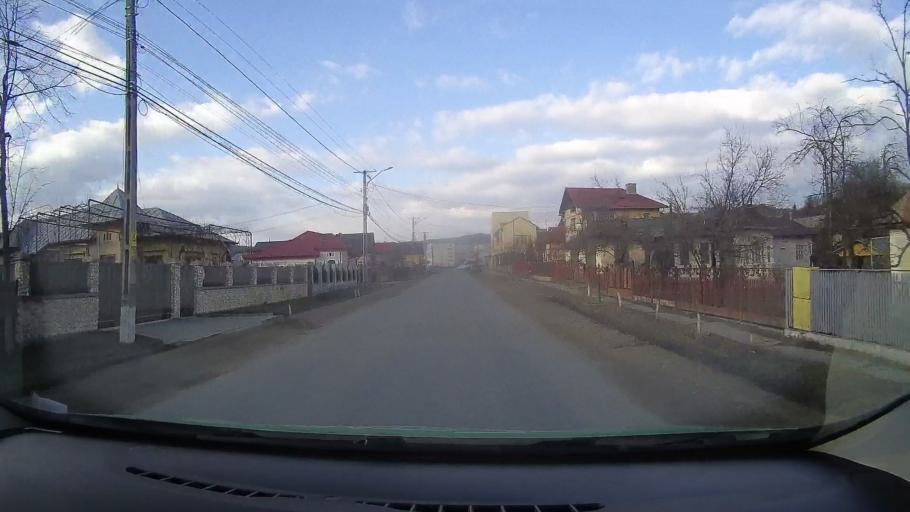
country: RO
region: Dambovita
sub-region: Comuna Ocnita
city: Ocnita
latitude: 44.9868
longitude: 25.5541
